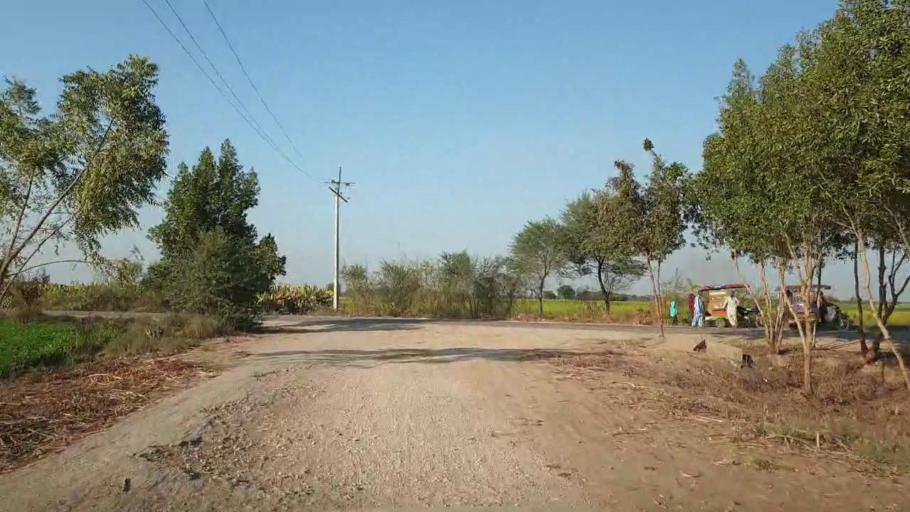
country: PK
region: Sindh
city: Tando Allahyar
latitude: 25.5017
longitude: 68.6491
